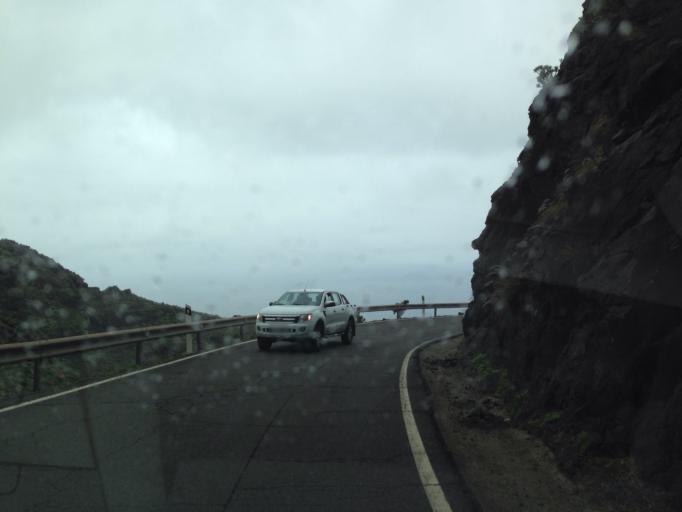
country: ES
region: Canary Islands
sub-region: Provincia de Las Palmas
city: San Nicolas
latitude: 28.0349
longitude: -15.7540
